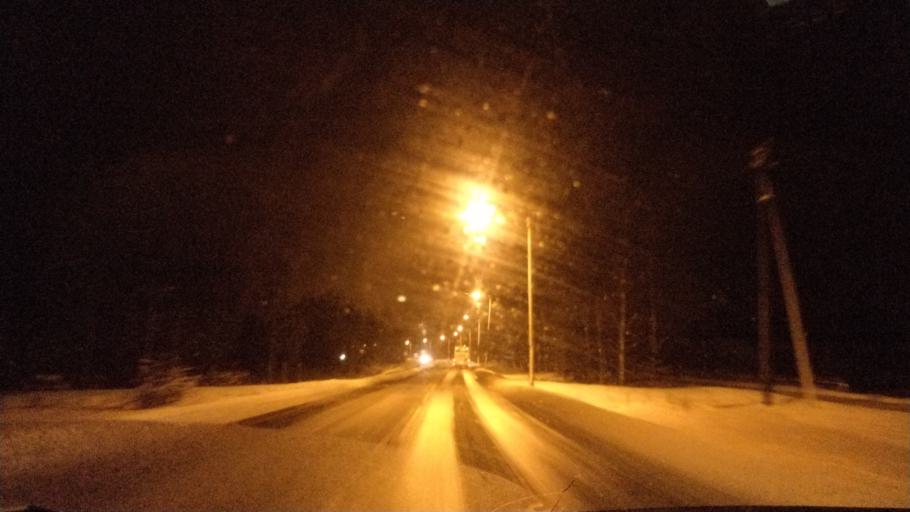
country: FI
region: Lapland
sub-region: Rovaniemi
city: Rovaniemi
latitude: 66.2879
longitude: 25.3458
